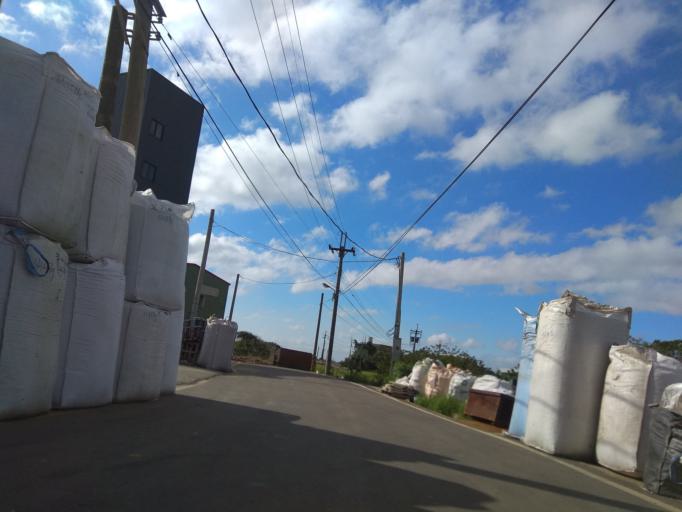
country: TW
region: Taiwan
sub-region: Hsinchu
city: Zhubei
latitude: 24.9719
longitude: 121.0735
